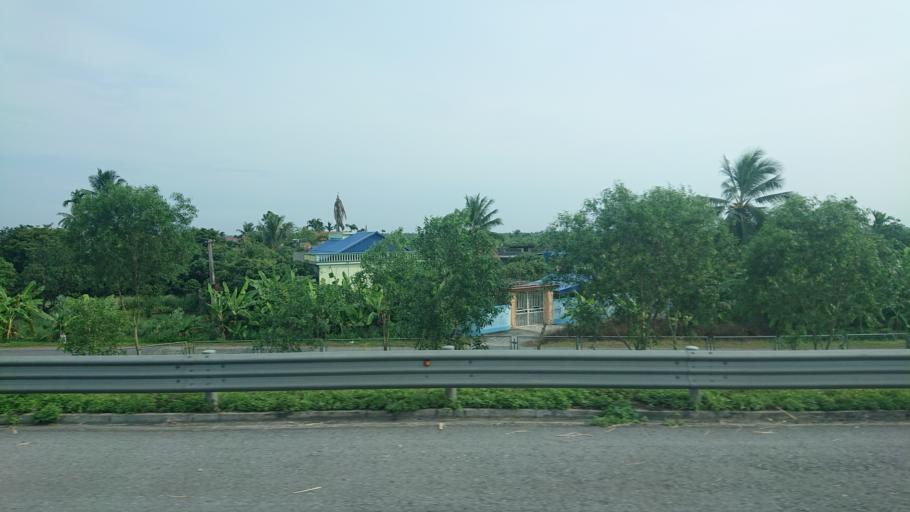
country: VN
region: Hai Duong
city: Tu Ky
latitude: 20.8208
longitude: 106.4770
